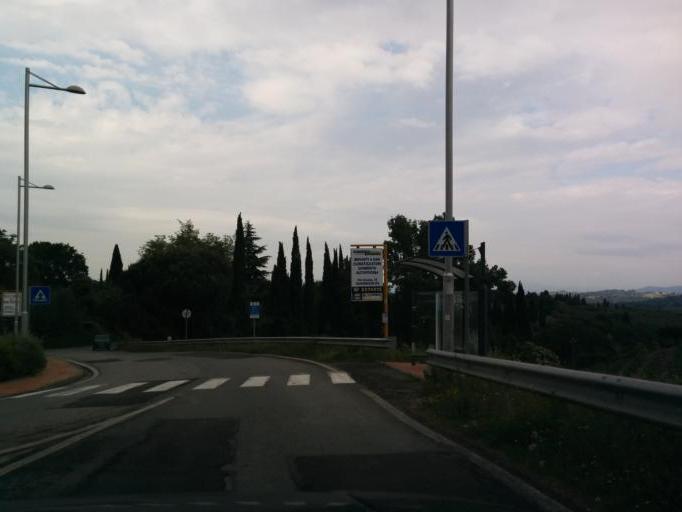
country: IT
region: Tuscany
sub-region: Province of Florence
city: San Casciano in Val di Pesa
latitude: 43.6624
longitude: 11.1914
